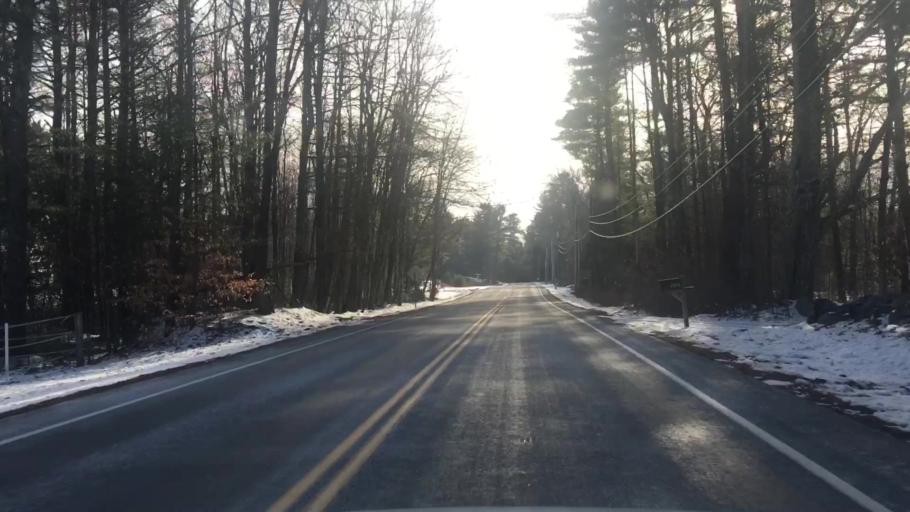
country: US
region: New Hampshire
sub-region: Merrimack County
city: East Concord
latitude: 43.2852
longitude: -71.5615
